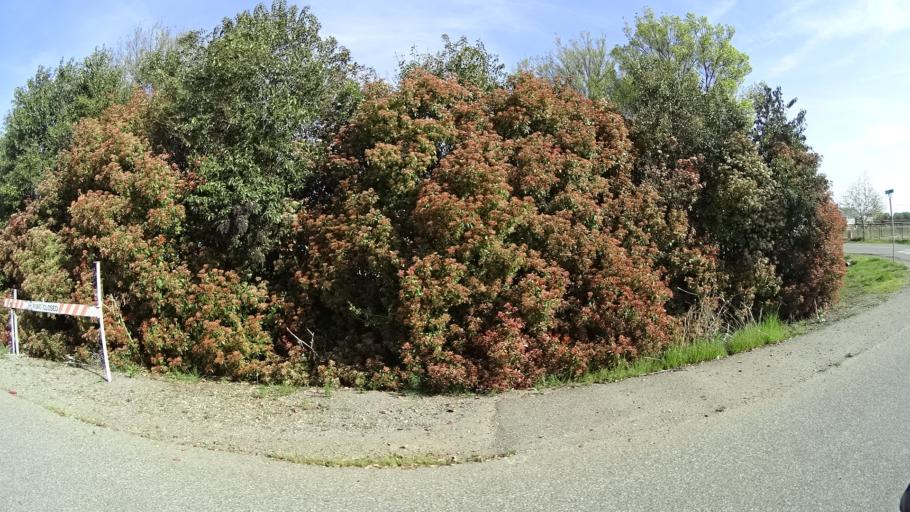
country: US
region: California
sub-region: Glenn County
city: Willows
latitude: 39.6114
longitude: -122.1957
